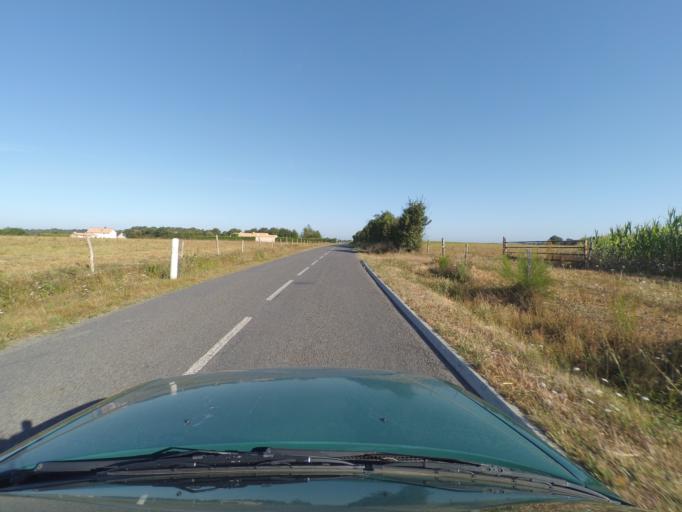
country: FR
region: Pays de la Loire
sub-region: Departement de la Loire-Atlantique
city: Le Bignon
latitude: 47.1071
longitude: -1.5113
